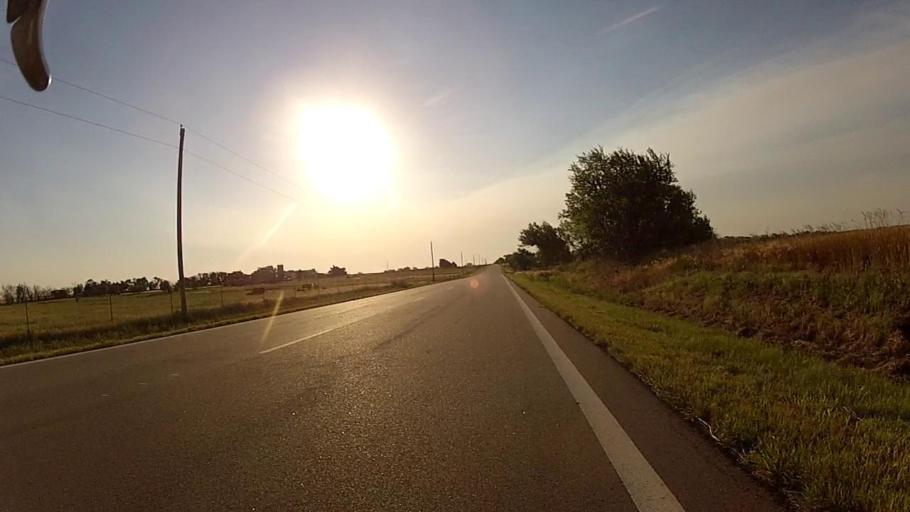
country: US
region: Kansas
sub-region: Sumner County
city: Caldwell
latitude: 37.1541
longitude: -97.7890
